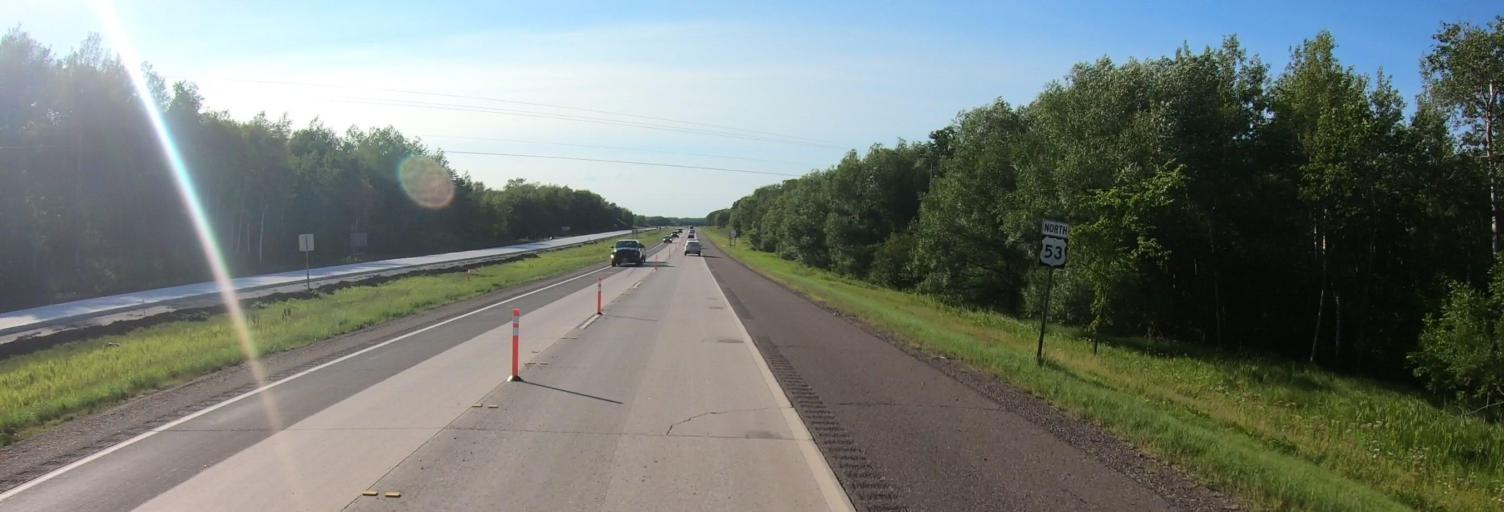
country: US
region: Minnesota
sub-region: Saint Louis County
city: Hermantown
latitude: 46.8621
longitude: -92.3222
